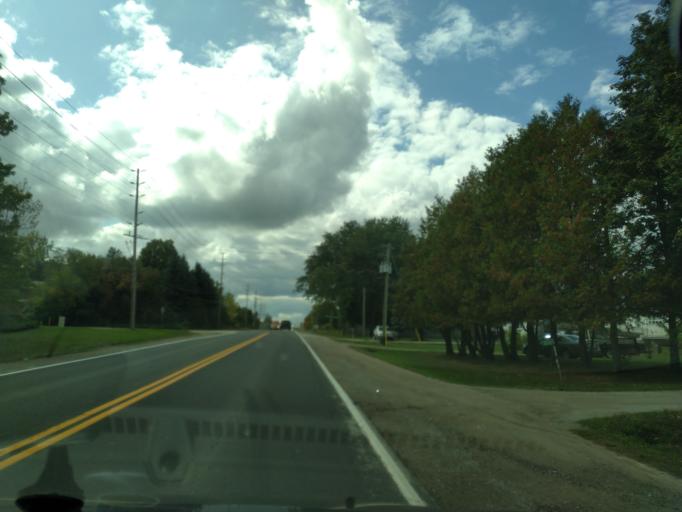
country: CA
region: Ontario
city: Innisfil
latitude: 44.2877
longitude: -79.6677
